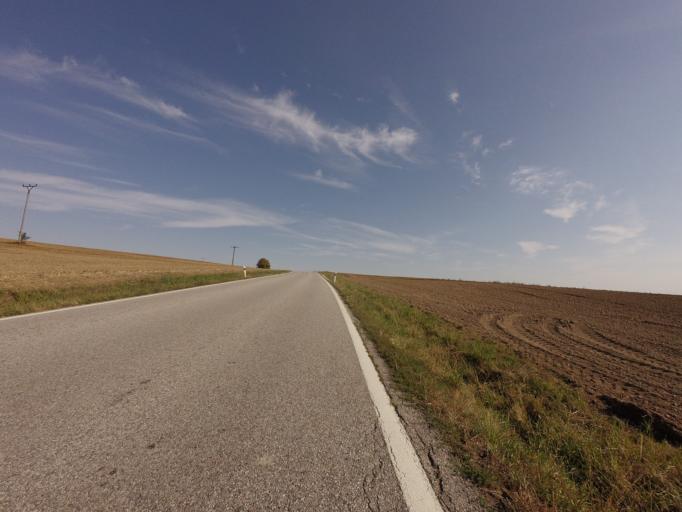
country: CZ
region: Jihocesky
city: Tyn nad Vltavou
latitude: 49.2858
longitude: 14.3958
